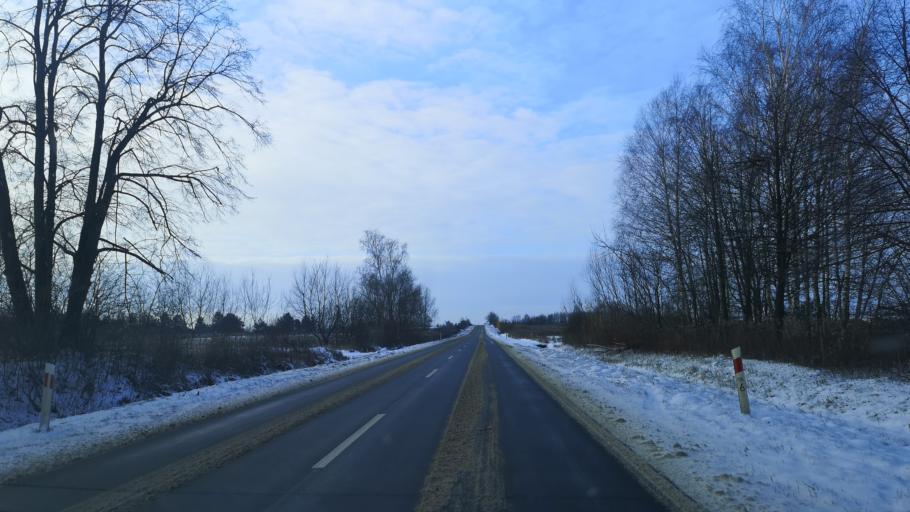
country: PL
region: Subcarpathian Voivodeship
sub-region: Powiat przeworski
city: Sieniawa
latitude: 50.2001
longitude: 22.6316
